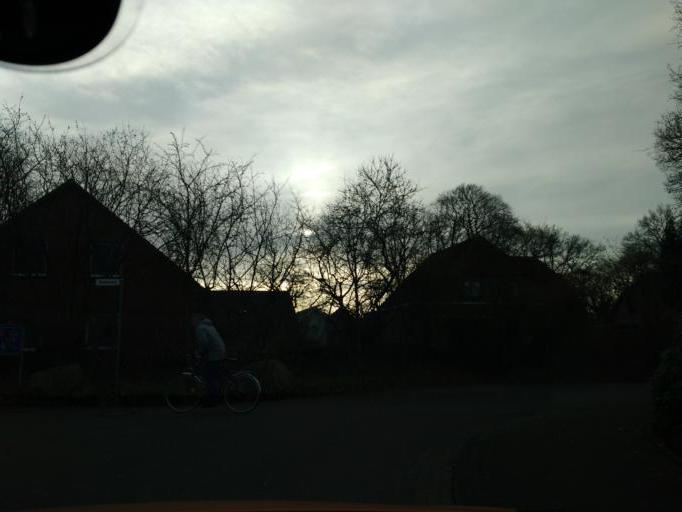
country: DE
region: Lower Saxony
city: Hude
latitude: 53.0962
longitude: 8.4621
